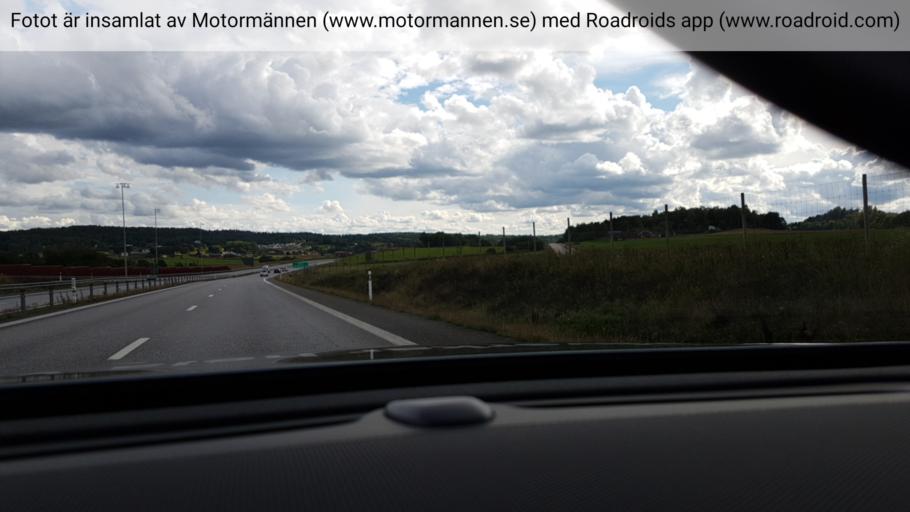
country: SE
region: Vaestra Goetaland
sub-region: Ale Kommun
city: Skepplanda
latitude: 57.9860
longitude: 12.1622
